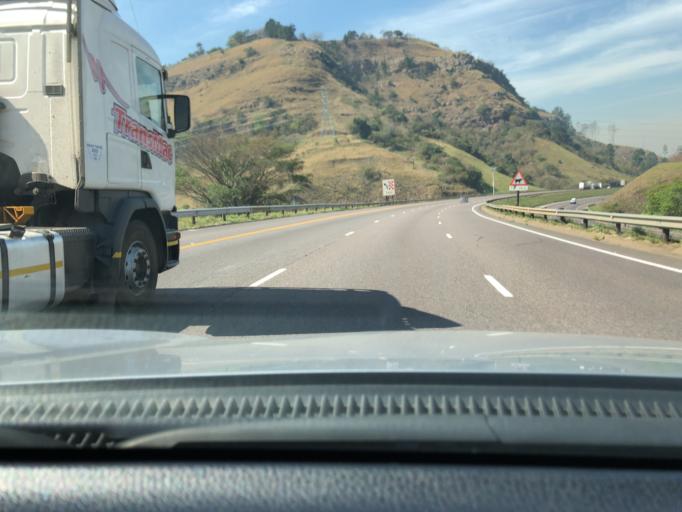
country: ZA
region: KwaZulu-Natal
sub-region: eThekwini Metropolitan Municipality
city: Mpumalanga
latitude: -29.8122
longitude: 30.7692
